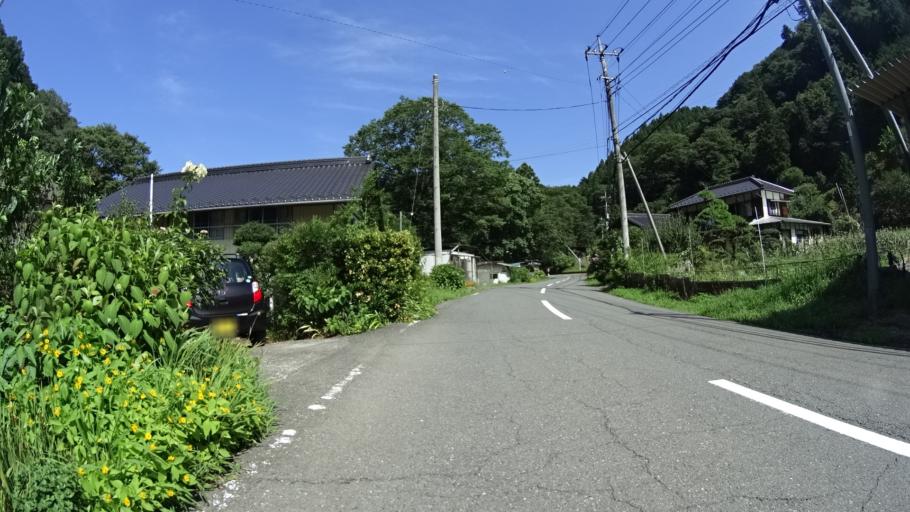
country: JP
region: Saitama
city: Chichibu
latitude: 36.0469
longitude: 138.8886
